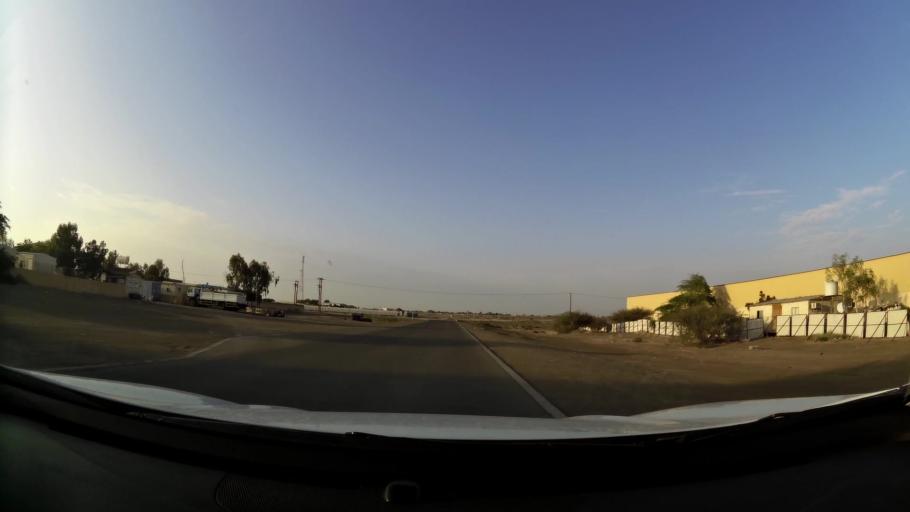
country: AE
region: Abu Dhabi
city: Al Ain
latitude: 24.1583
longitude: 55.8217
